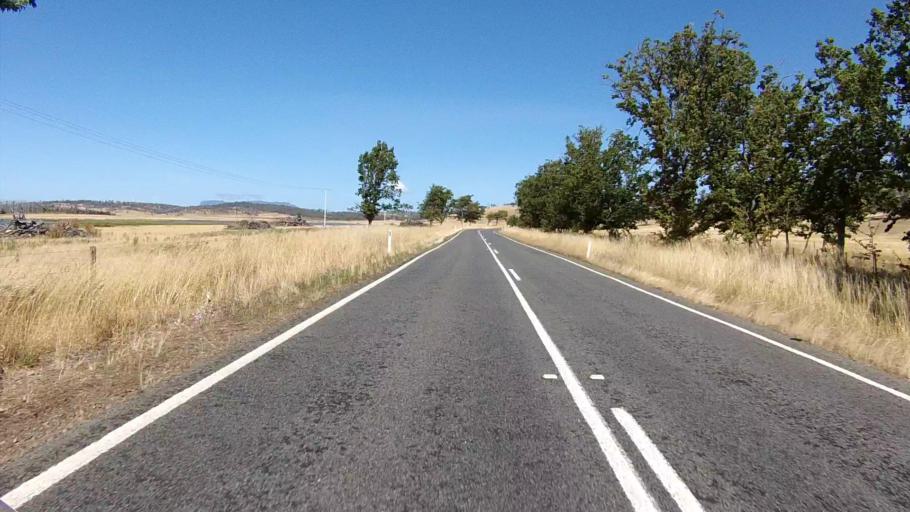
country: AU
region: Tasmania
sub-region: Sorell
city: Sorell
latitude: -42.4810
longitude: 147.9325
